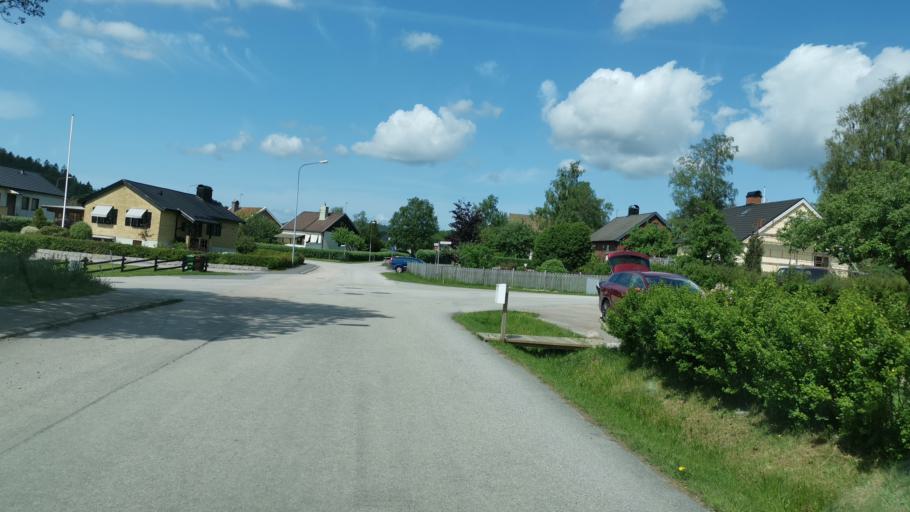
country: SE
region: Vaestra Goetaland
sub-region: Uddevalla Kommun
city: Uddevalla
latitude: 58.3533
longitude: 11.8431
